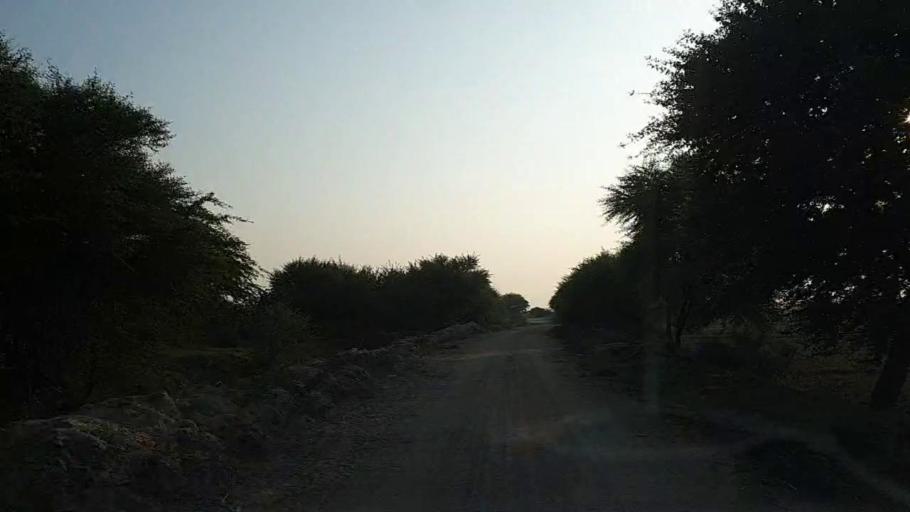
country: PK
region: Sindh
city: Daro Mehar
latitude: 24.7398
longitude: 68.1838
